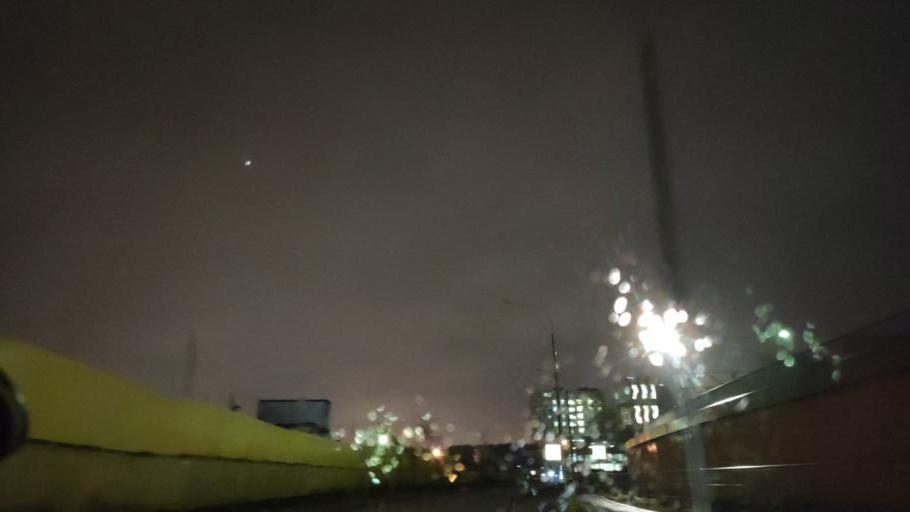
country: RU
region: Moskovskaya
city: Marfino
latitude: 55.6988
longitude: 37.3878
